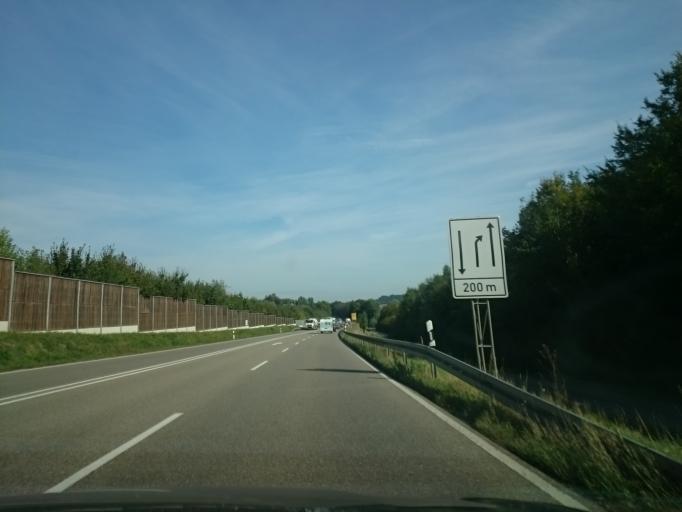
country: DE
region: Bavaria
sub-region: Swabia
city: Aichach
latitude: 48.4526
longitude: 11.1450
